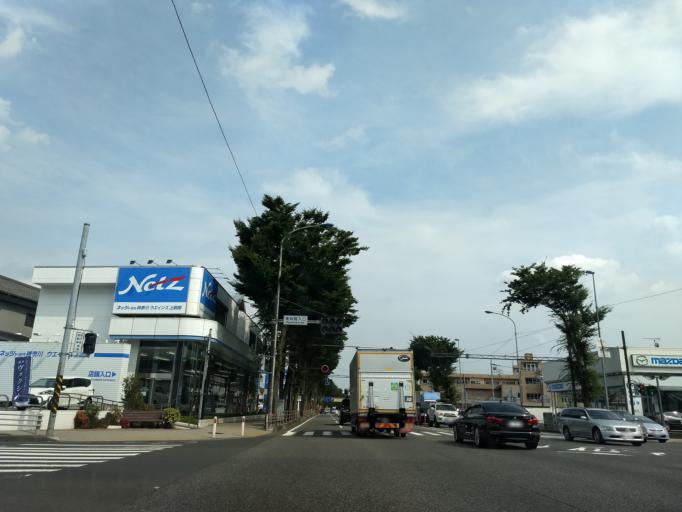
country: JP
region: Tokyo
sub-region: Machida-shi
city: Machida
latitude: 35.5298
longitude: 139.4439
